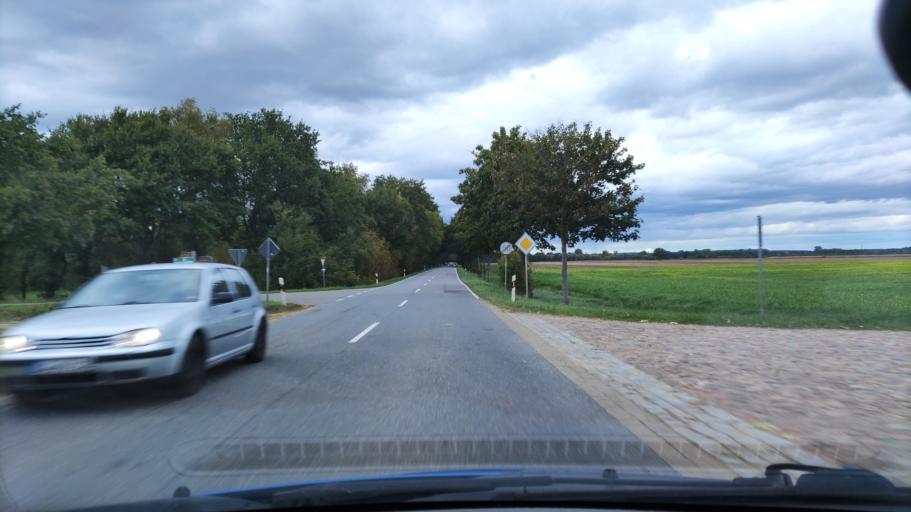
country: DE
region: Lower Saxony
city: Neu Darchau
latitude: 53.3213
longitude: 10.9527
